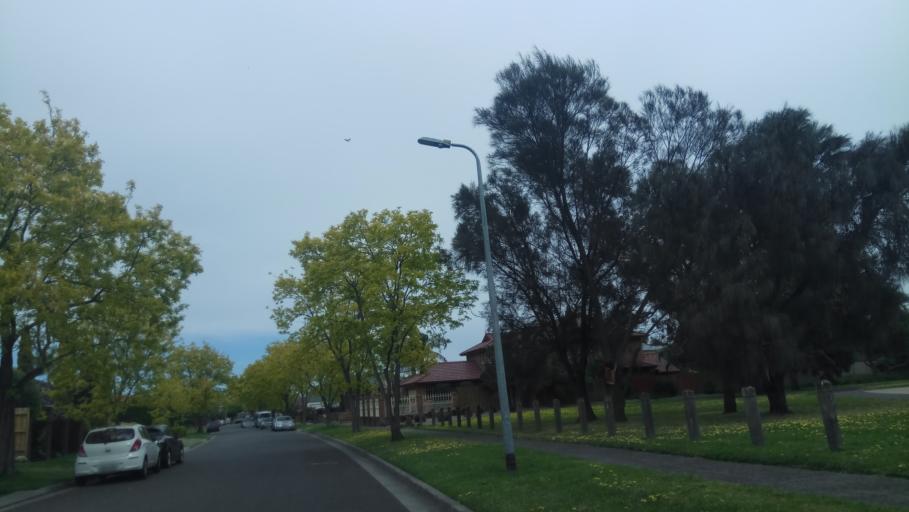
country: AU
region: Victoria
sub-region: Kingston
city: Dingley Village
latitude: -37.9699
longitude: 145.1282
